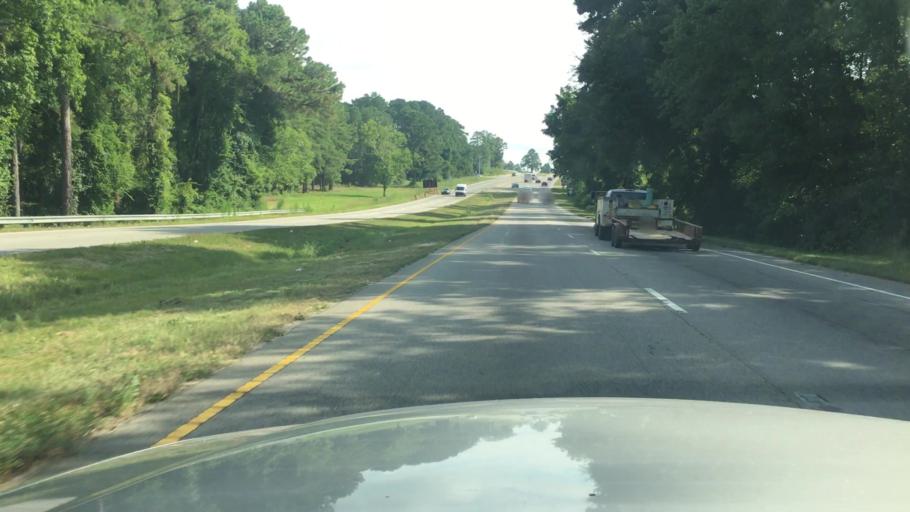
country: US
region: North Carolina
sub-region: Cumberland County
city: Hope Mills
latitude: 34.9659
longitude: -78.9158
